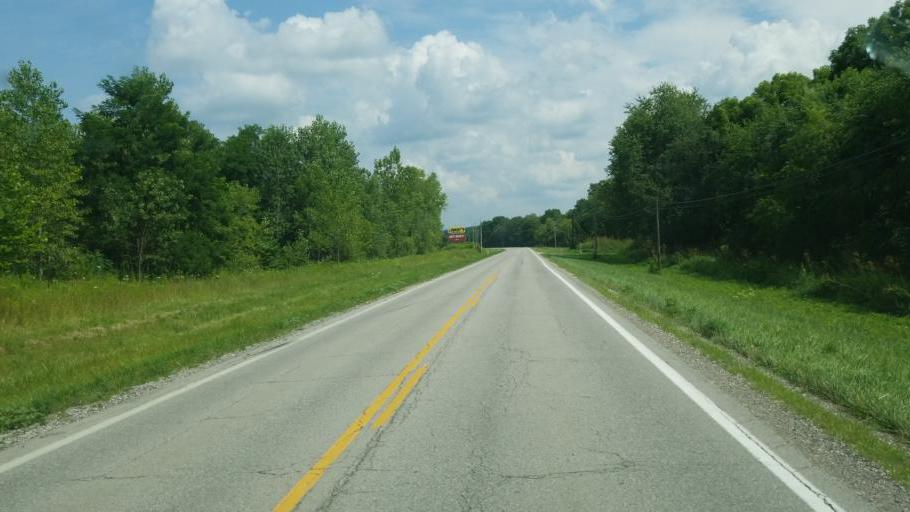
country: US
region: Ohio
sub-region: Sandusky County
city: Bellville
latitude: 40.6142
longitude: -82.4954
